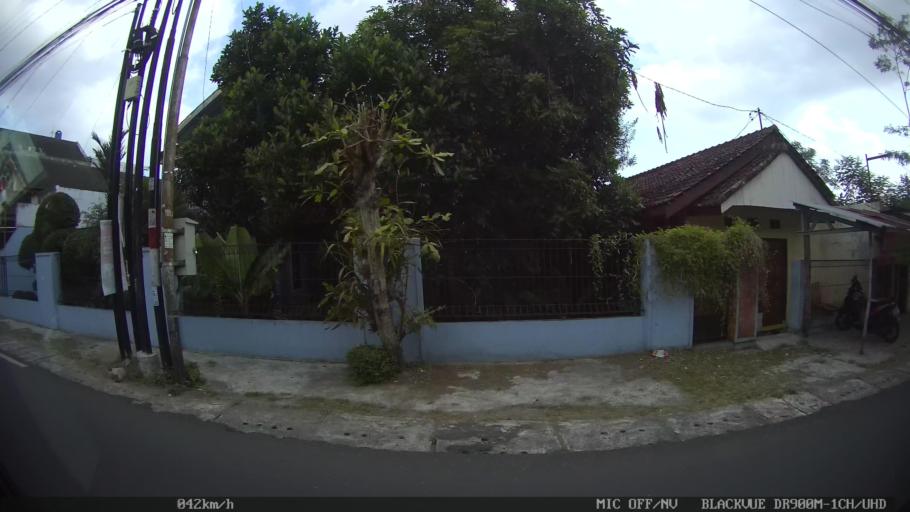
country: ID
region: Daerah Istimewa Yogyakarta
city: Gamping Lor
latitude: -7.7832
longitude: 110.3384
